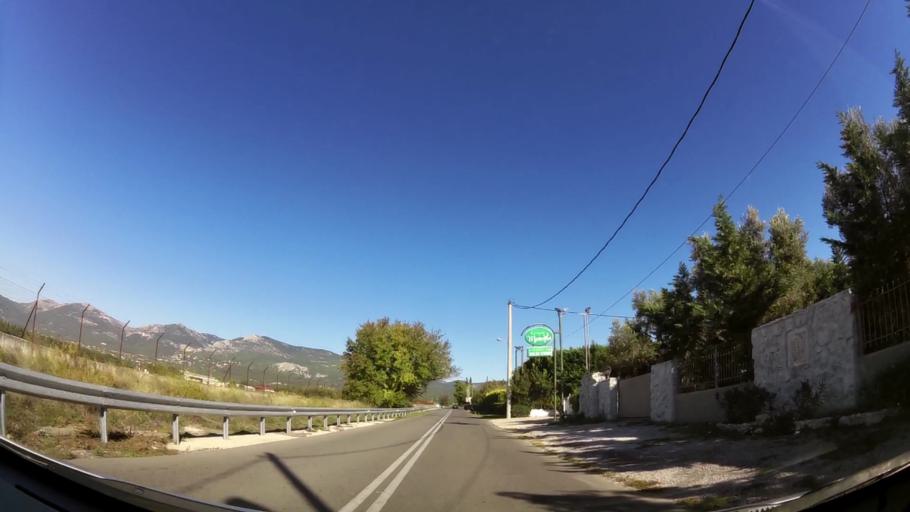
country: GR
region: Attica
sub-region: Nomarchia Anatolikis Attikis
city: Varybobi
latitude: 38.1128
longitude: 23.7900
